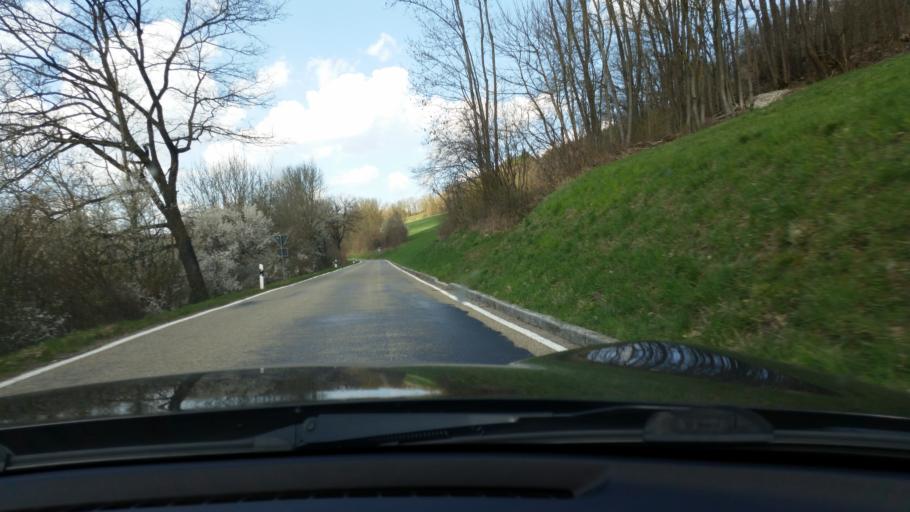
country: DE
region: Baden-Wuerttemberg
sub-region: Regierungsbezirk Stuttgart
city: Langenburg
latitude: 49.2654
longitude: 9.8417
